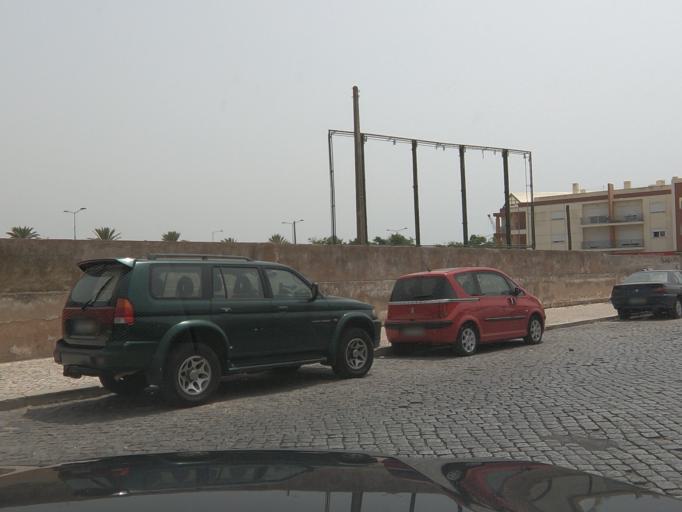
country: PT
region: Faro
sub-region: Portimao
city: Portimao
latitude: 37.1337
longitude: -8.5364
